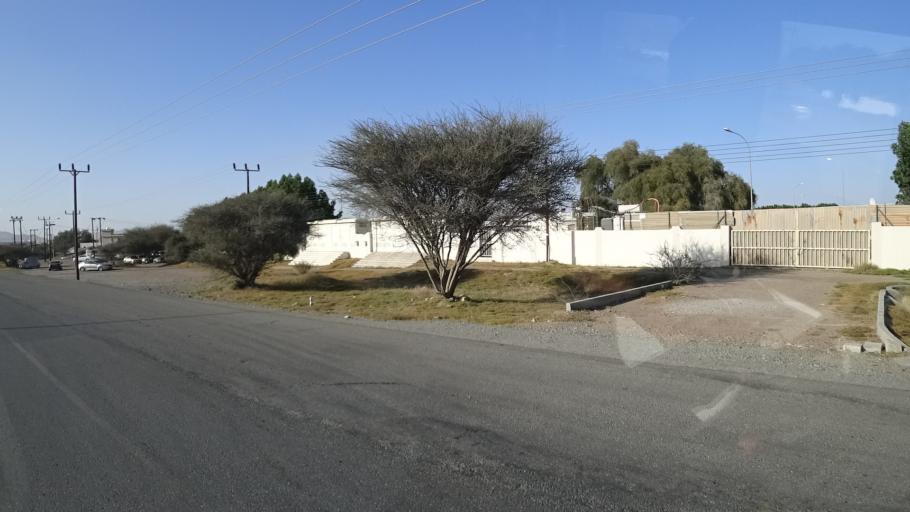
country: OM
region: Muhafazat ad Dakhiliyah
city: Bidbid
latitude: 23.4858
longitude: 58.1997
